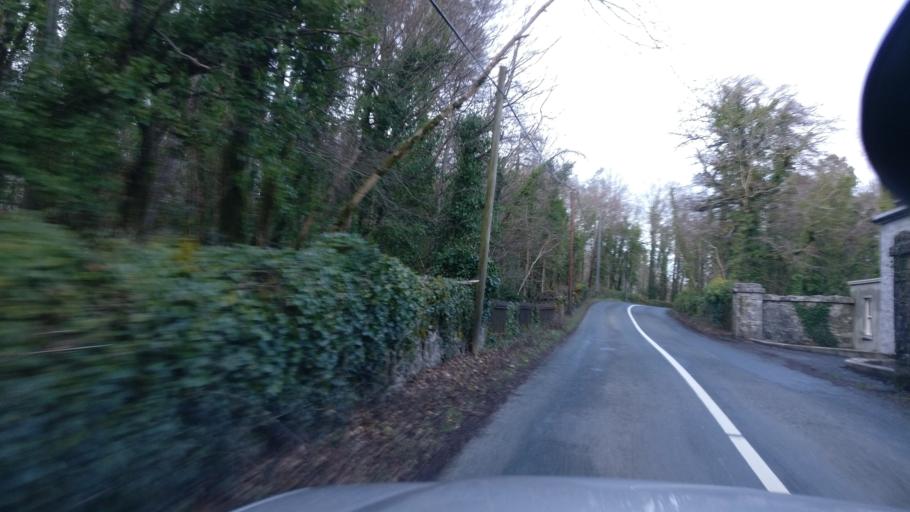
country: IE
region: Connaught
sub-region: Maigh Eo
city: Ballinrobe
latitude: 53.5419
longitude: -9.2964
